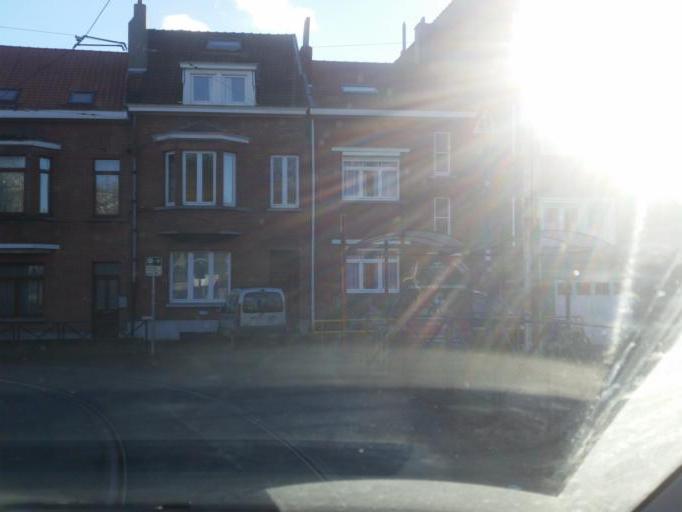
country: BE
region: Flanders
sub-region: Provincie Vlaams-Brabant
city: Linkebeek
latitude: 50.7944
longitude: 4.3627
